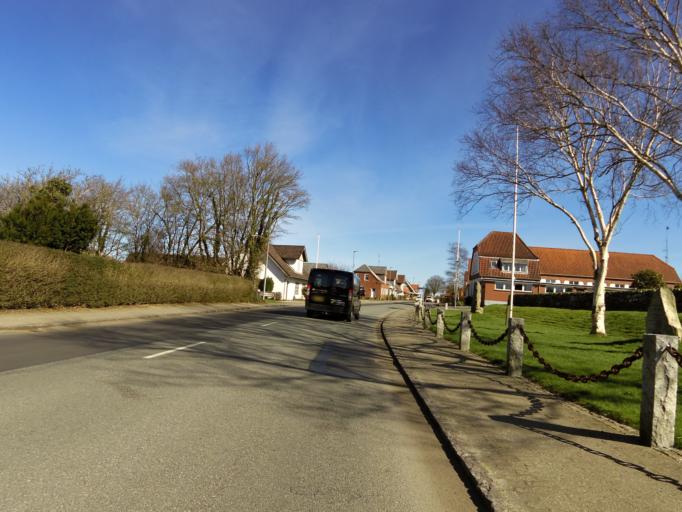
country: DK
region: South Denmark
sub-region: Vejen Kommune
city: Rodding
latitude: 55.3536
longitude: 8.9781
